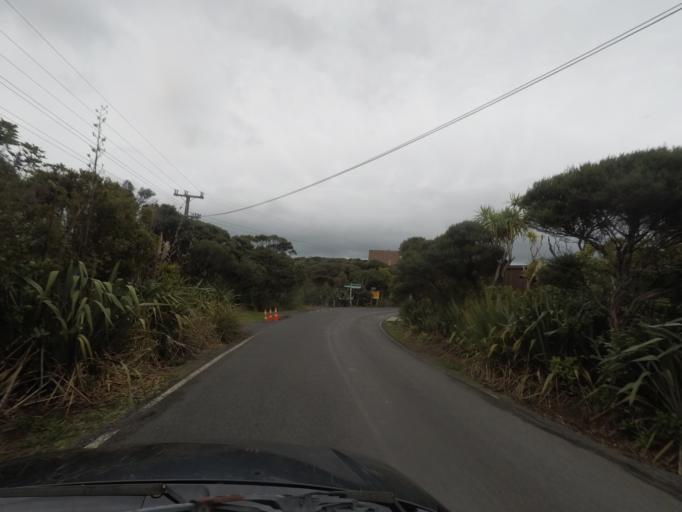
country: NZ
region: Auckland
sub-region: Auckland
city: Muriwai Beach
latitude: -36.9697
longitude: 174.4748
